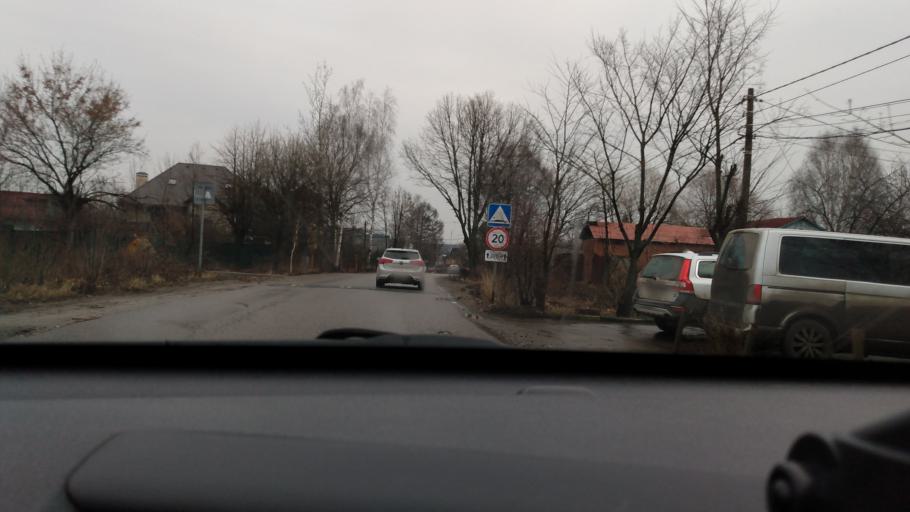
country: RU
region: Moscow
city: Zagor'ye
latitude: 55.5484
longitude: 37.6556
